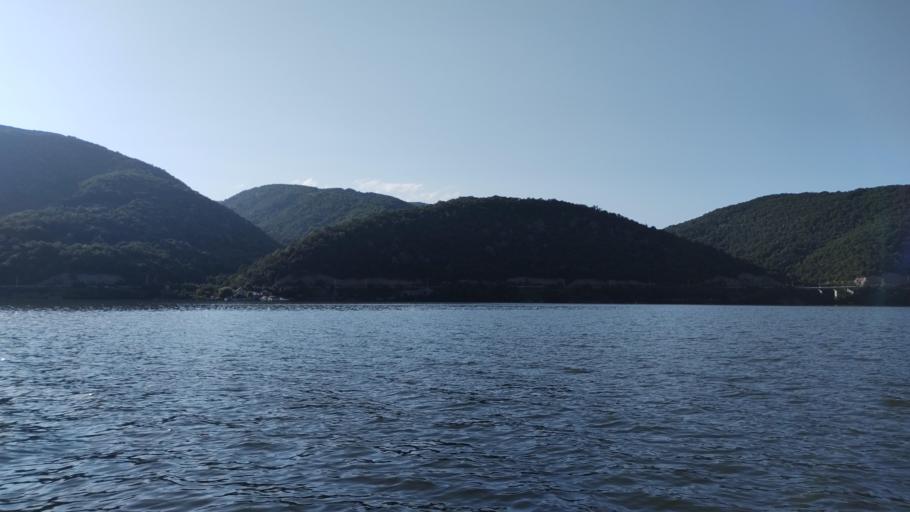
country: RO
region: Mehedinti
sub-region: Comuna Dubova
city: Dubova
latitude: 44.5776
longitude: 22.2464
